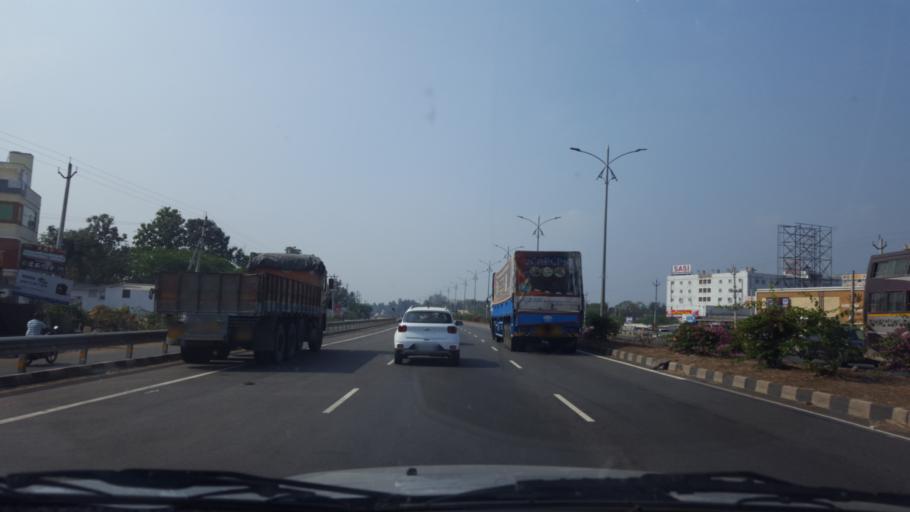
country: IN
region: Andhra Pradesh
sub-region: Vishakhapatnam
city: Bhimunipatnam
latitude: 17.9196
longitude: 83.4168
